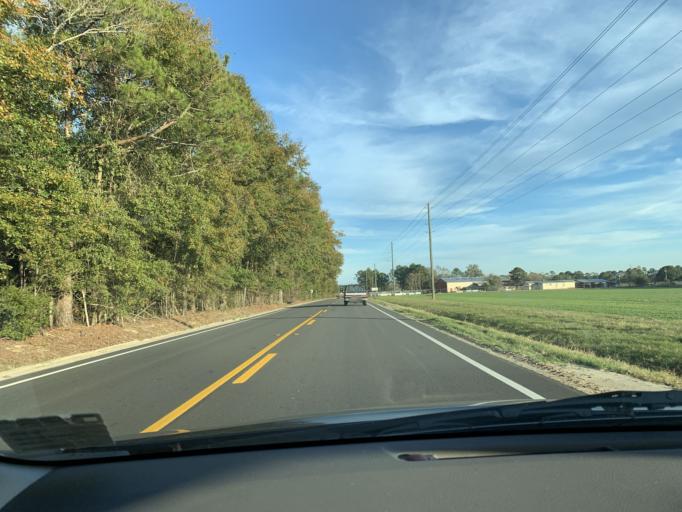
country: US
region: Georgia
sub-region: Irwin County
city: Ocilla
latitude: 31.5917
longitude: -83.0994
